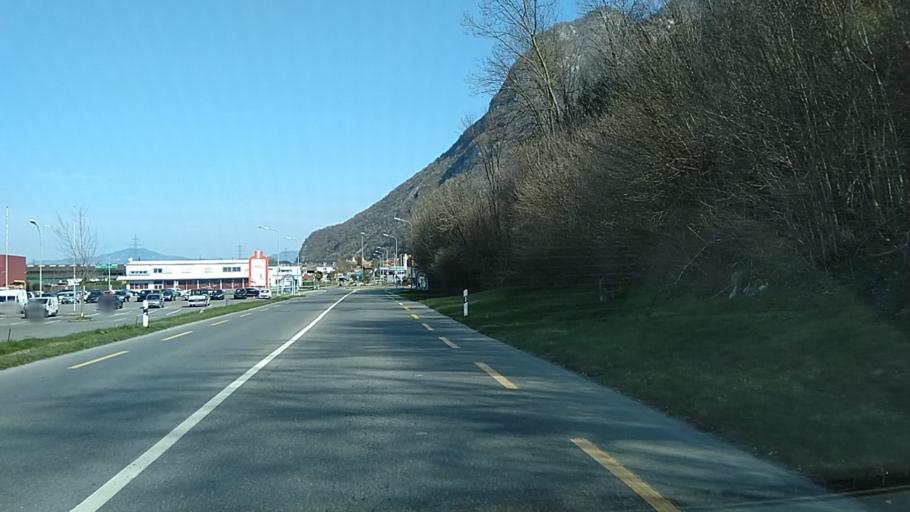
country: CH
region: Valais
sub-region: Monthey District
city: Vouvry
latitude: 46.3524
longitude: 6.9333
